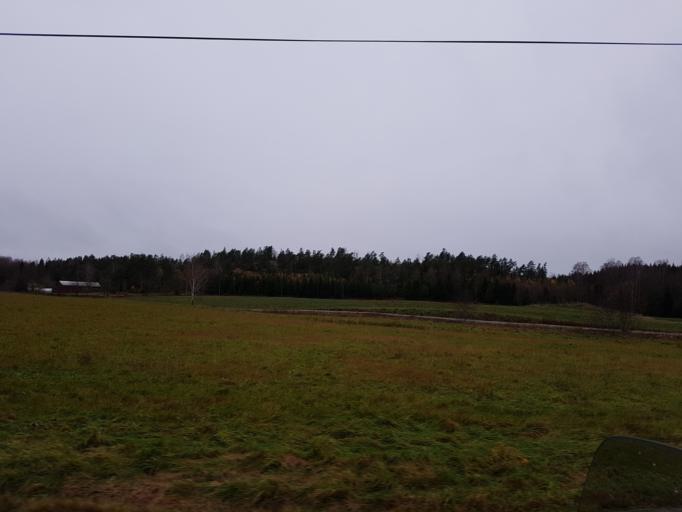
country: SE
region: Vaestra Goetaland
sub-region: Orust
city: Henan
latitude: 58.2218
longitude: 11.7339
